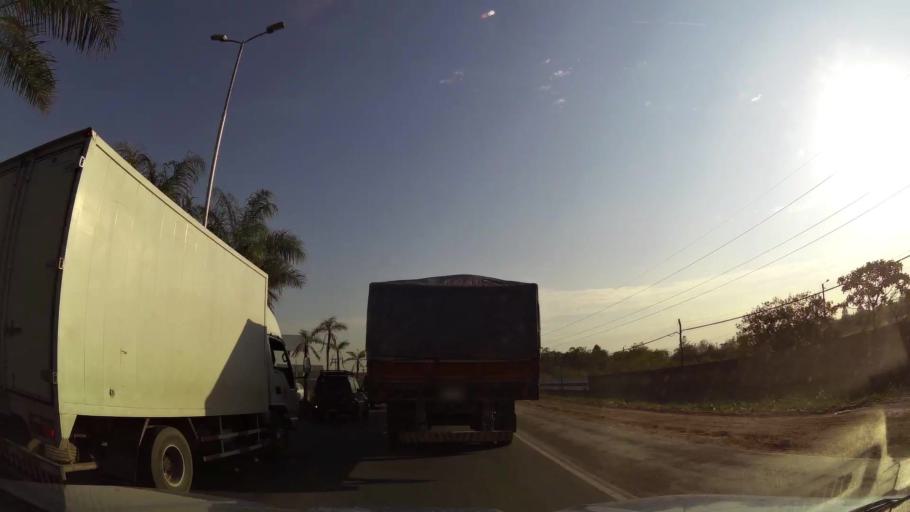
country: BO
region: Santa Cruz
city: Santa Cruz de la Sierra
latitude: -17.7026
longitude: -63.1598
